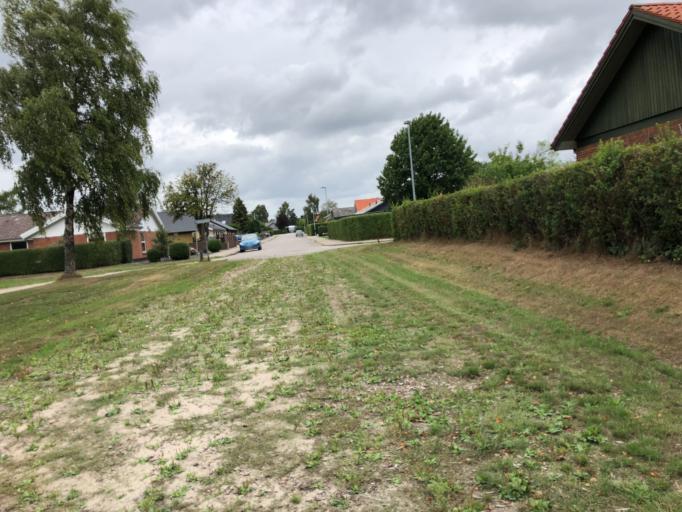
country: DK
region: Central Jutland
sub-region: Herning Kommune
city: Lind
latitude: 56.0618
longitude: 8.9888
